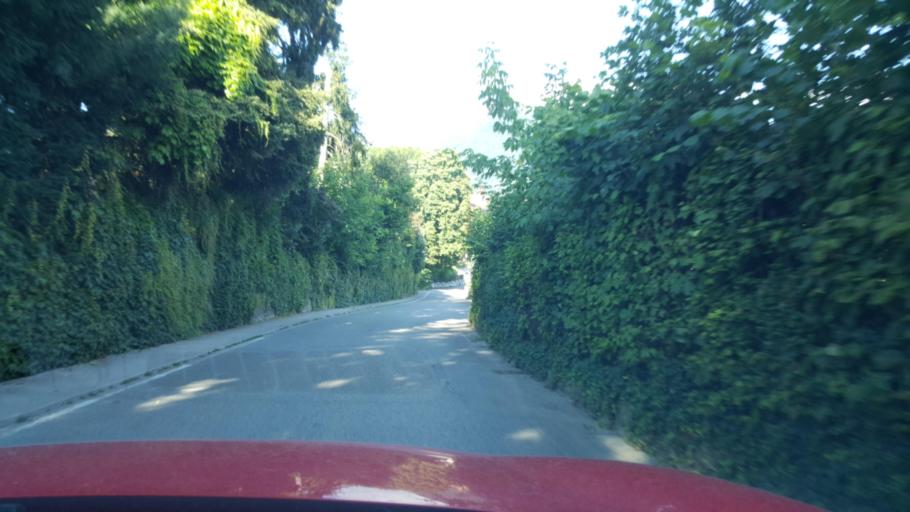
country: FR
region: Rhone-Alpes
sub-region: Departement de la Haute-Savoie
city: Menthon-Saint-Bernard
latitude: 45.8568
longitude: 6.1924
